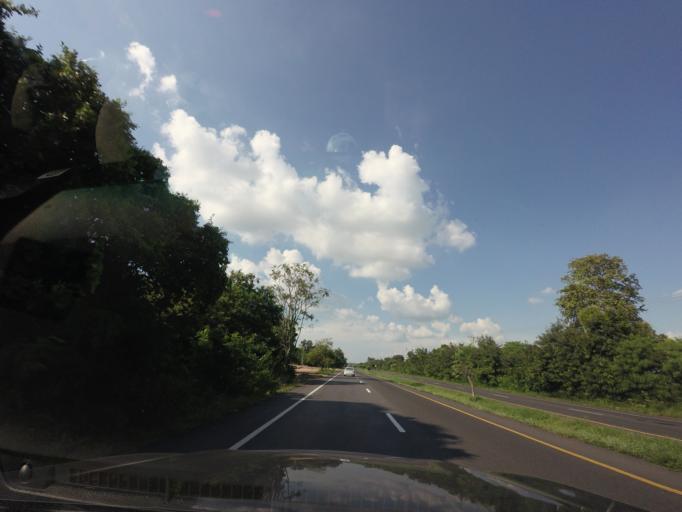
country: TH
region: Nakhon Ratchasima
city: Bua Lai
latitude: 15.6722
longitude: 102.5754
